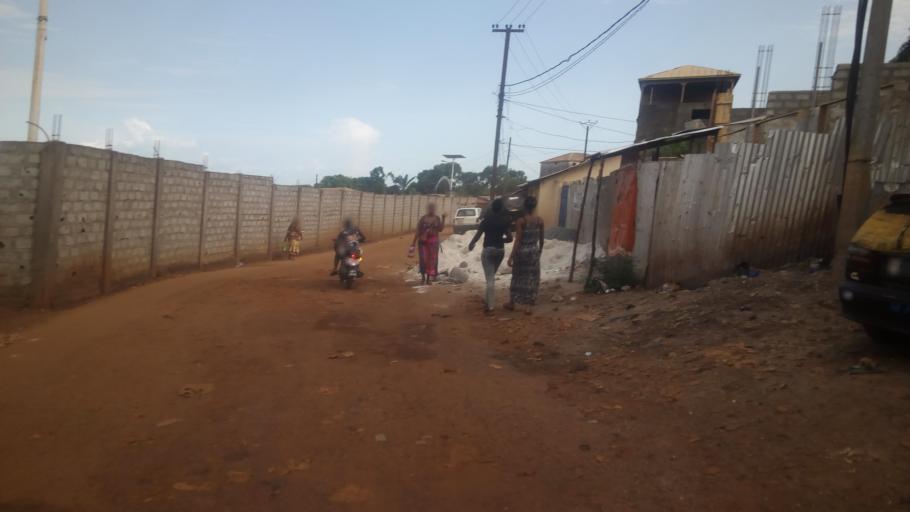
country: GN
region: Kindia
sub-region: Prefecture de Dubreka
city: Dubreka
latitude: 9.6570
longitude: -13.5354
